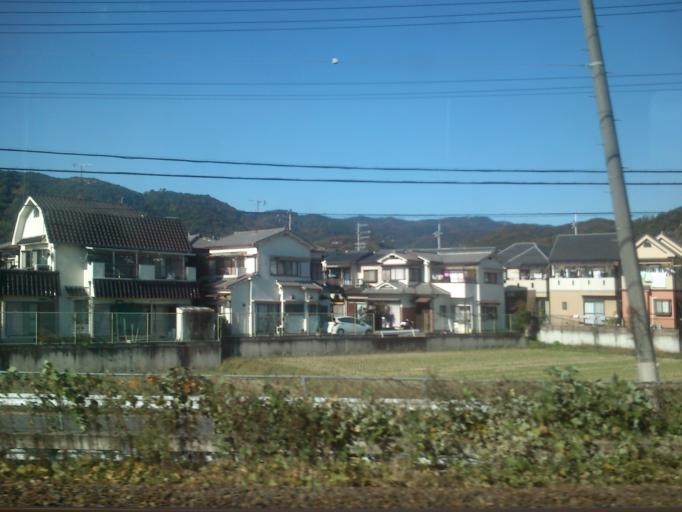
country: JP
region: Kyoto
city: Yawata
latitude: 34.8869
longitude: 135.6684
